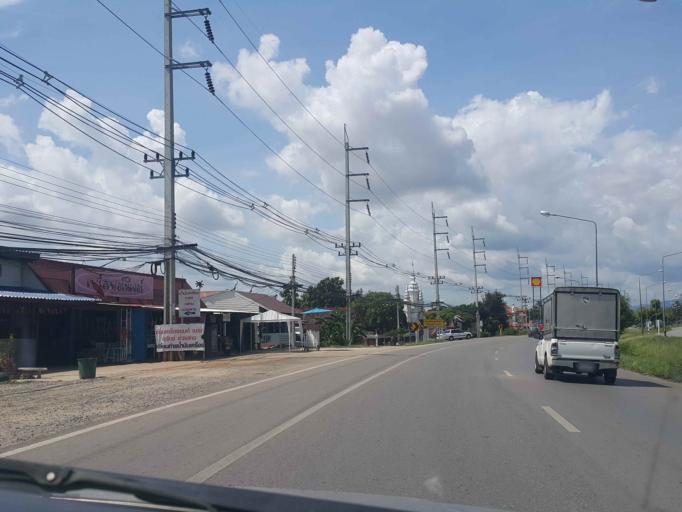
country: TH
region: Phayao
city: Phayao
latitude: 19.1585
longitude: 99.9144
